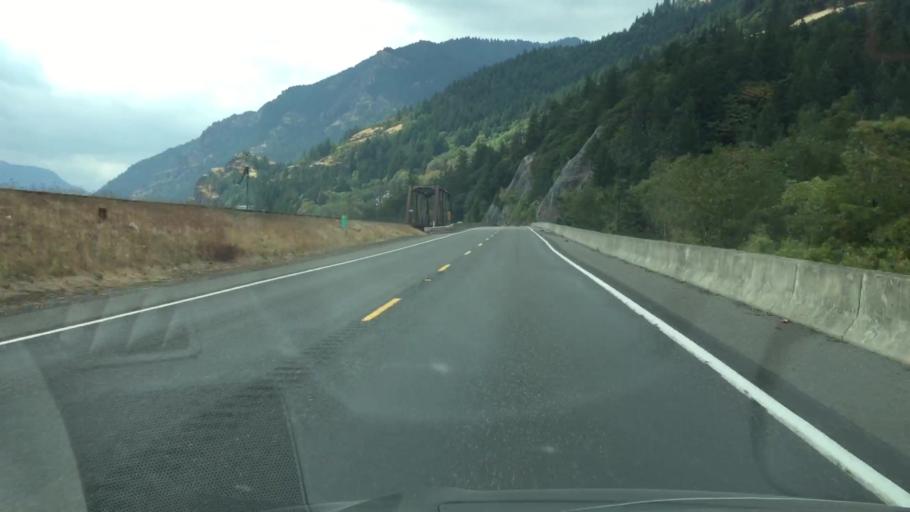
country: US
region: Oregon
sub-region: Hood River County
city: Hood River
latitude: 45.7110
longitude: -121.6462
